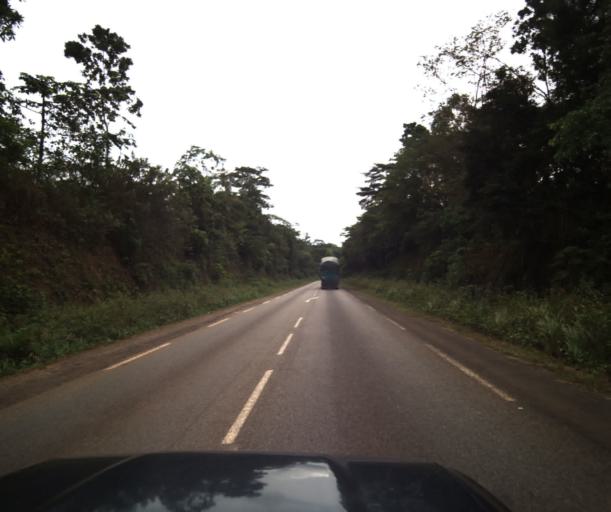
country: CM
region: Littoral
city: Edea
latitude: 3.8216
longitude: 10.3784
